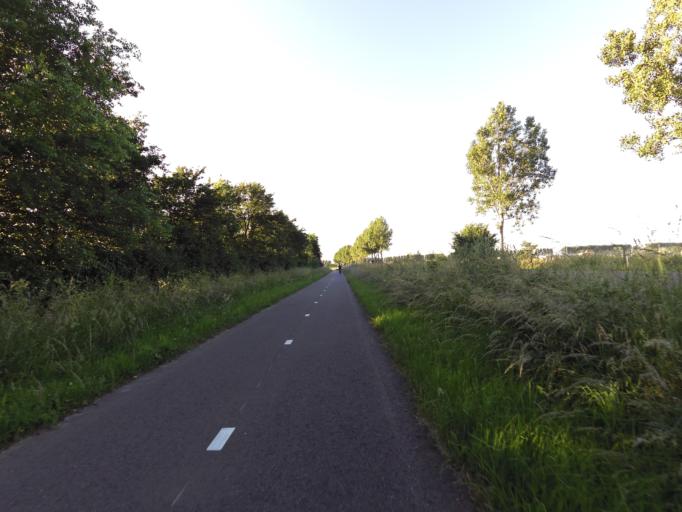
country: NL
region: Gelderland
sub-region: Gemeente Zevenaar
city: Zevenaar
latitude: 51.9639
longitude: 6.0857
